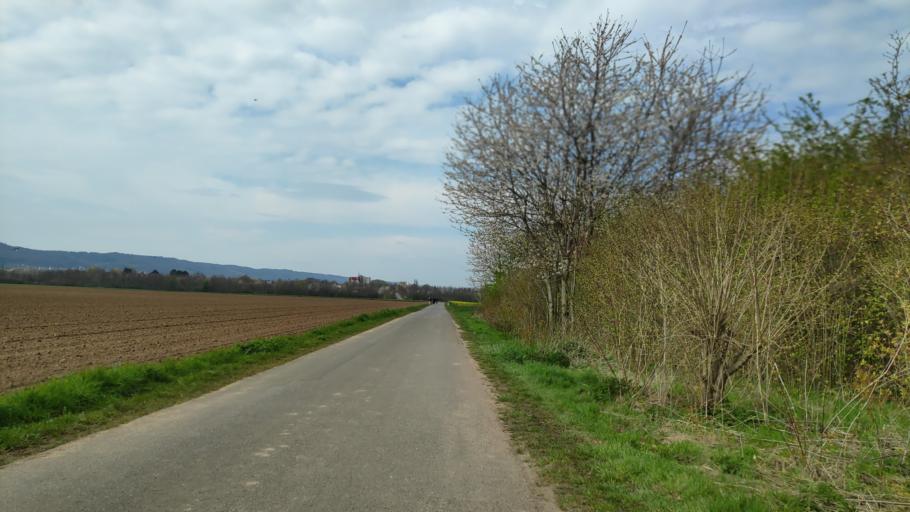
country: DE
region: North Rhine-Westphalia
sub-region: Regierungsbezirk Detmold
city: Minden
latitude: 52.2734
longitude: 8.9183
